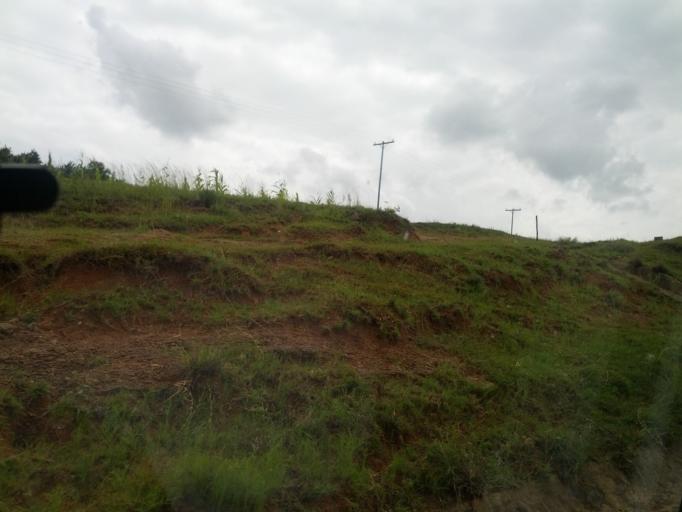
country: LS
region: Leribe
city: Leribe
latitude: -29.0229
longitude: 28.2253
